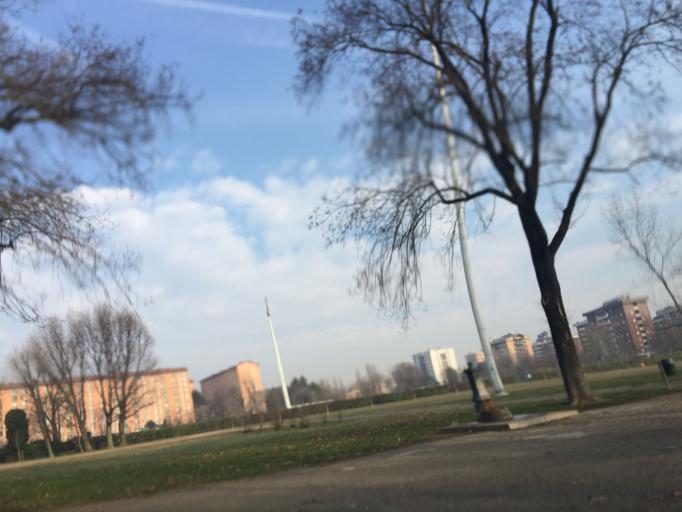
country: IT
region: Lombardy
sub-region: Citta metropolitana di Milano
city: Romano Banco
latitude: 45.4361
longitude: 9.1416
